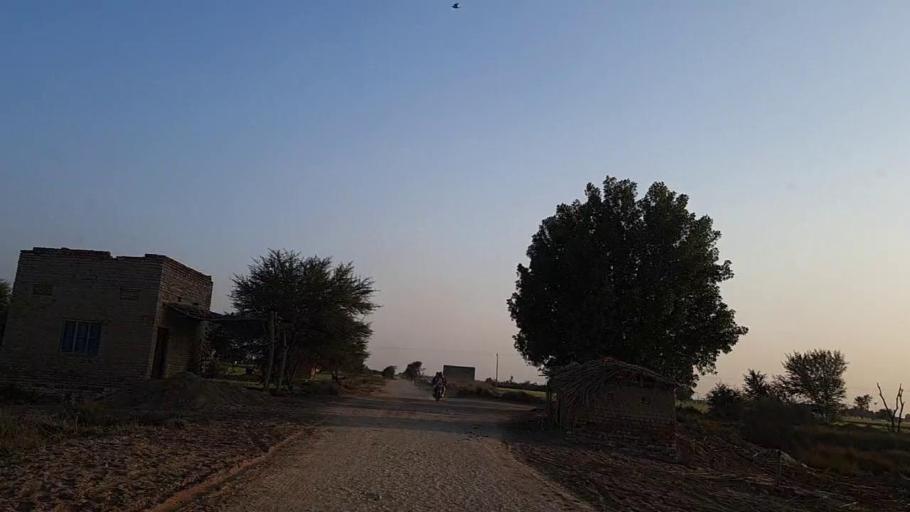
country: PK
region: Sindh
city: Shahdadpur
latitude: 26.0007
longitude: 68.4928
